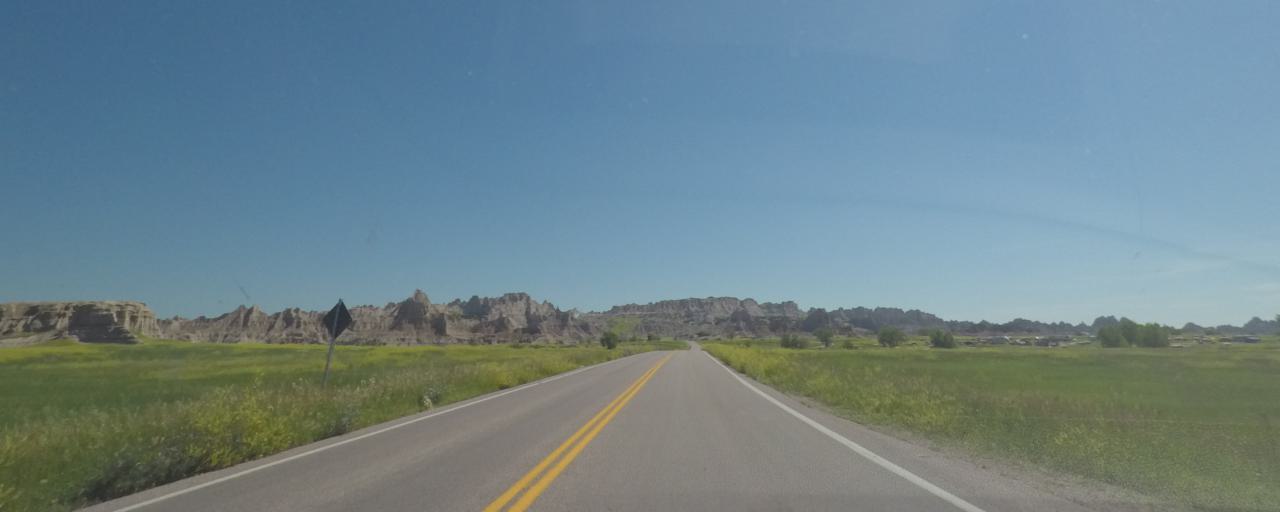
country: US
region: South Dakota
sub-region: Haakon County
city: Philip
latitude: 43.7429
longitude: -101.9556
